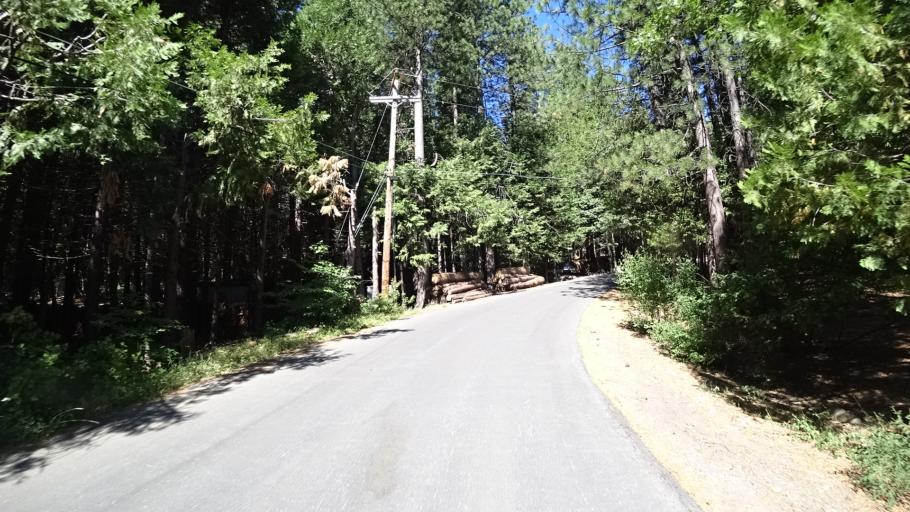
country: US
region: California
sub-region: Calaveras County
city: Arnold
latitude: 38.2874
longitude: -120.2723
